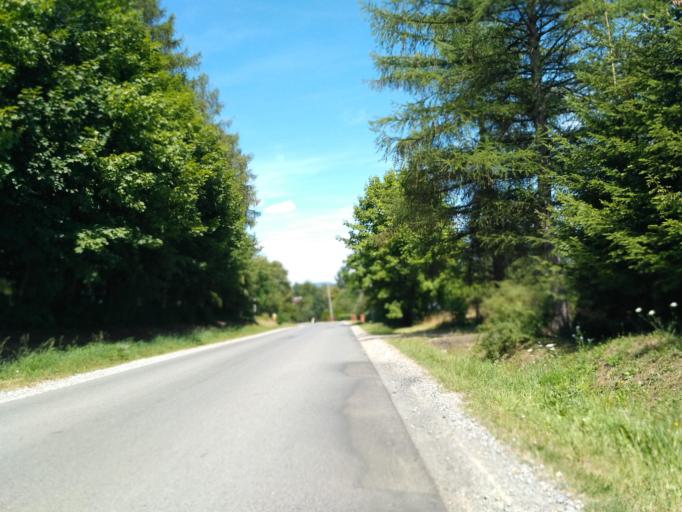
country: PL
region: Subcarpathian Voivodeship
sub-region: Powiat sanocki
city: Nowosielce-Gniewosz
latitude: 49.5241
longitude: 22.1038
